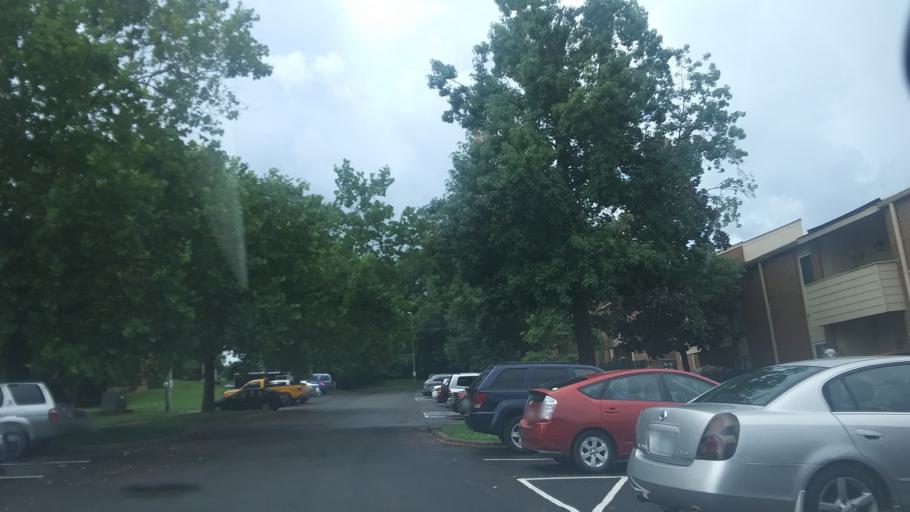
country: US
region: Tennessee
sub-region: Davidson County
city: Belle Meade
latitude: 36.1565
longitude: -86.8867
